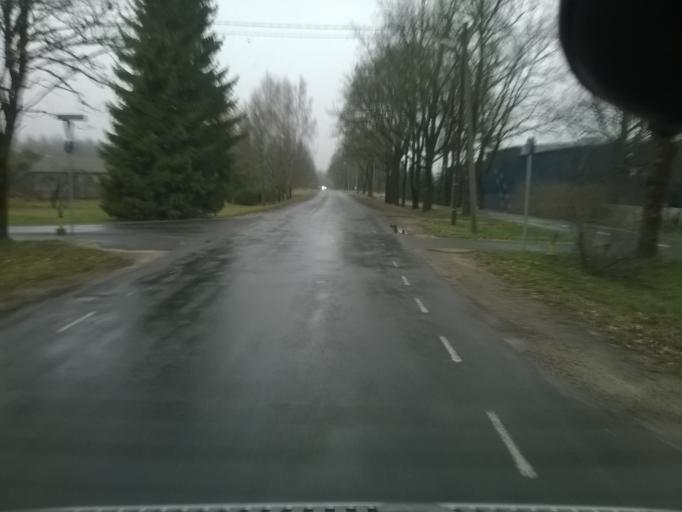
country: EE
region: Raplamaa
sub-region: Kohila vald
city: Kohila
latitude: 59.1618
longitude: 24.6508
